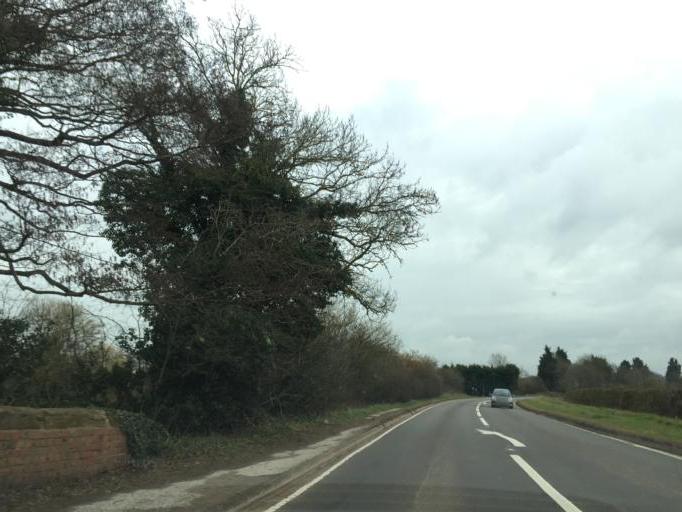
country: GB
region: England
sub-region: Warwickshire
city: Henley in Arden
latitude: 52.2864
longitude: -1.7478
